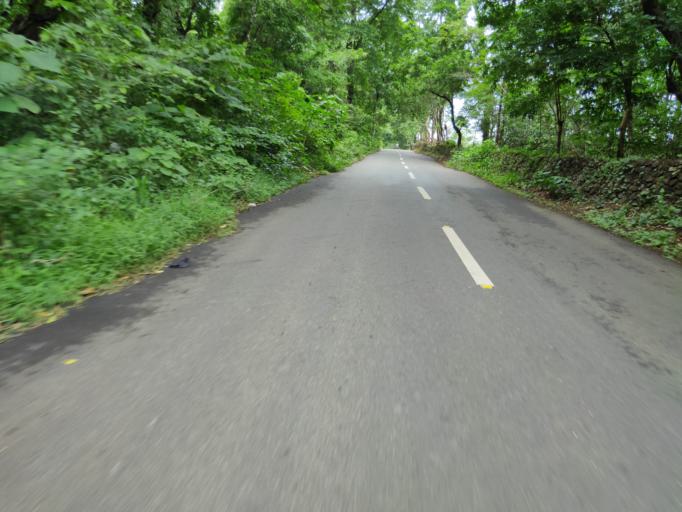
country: IN
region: Kerala
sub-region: Malappuram
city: Manjeri
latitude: 11.2275
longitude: 76.2507
